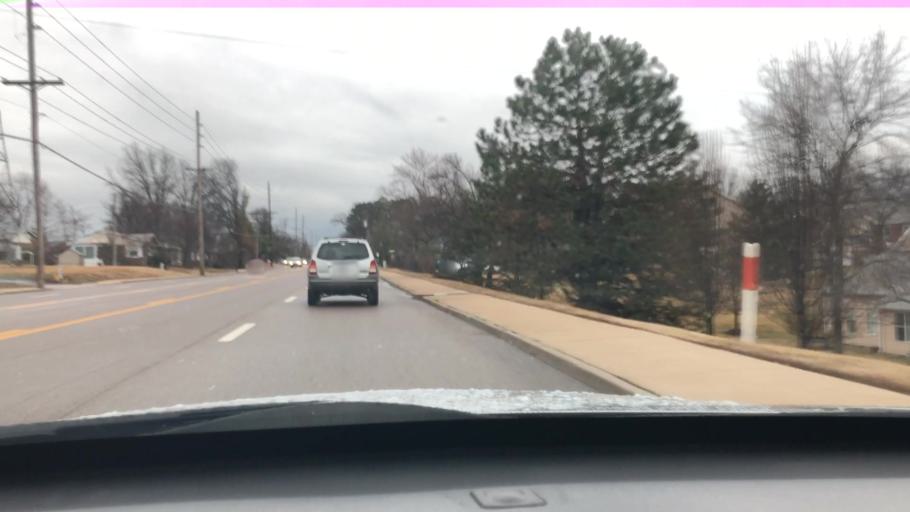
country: US
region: Missouri
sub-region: Saint Louis County
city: Valley Park
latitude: 38.5678
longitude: -90.5087
